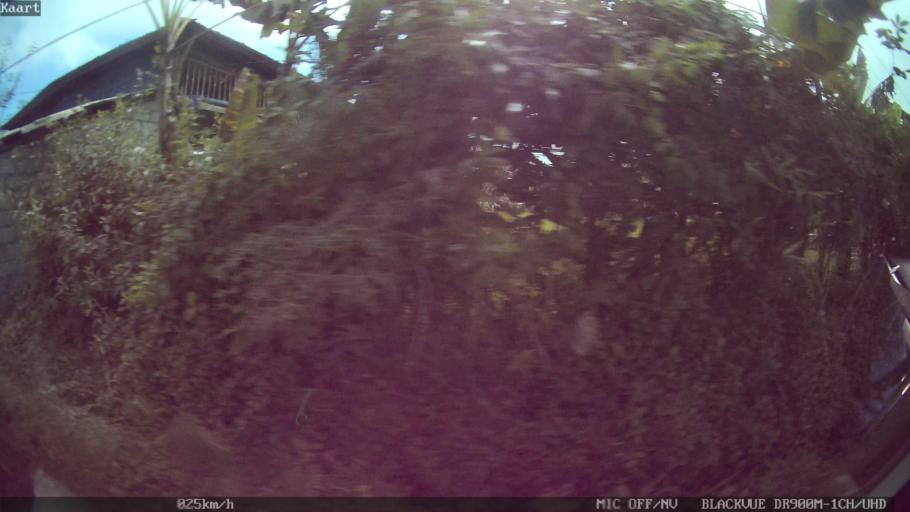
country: ID
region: Bali
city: Banjar Abuan
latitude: -8.4670
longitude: 115.3412
